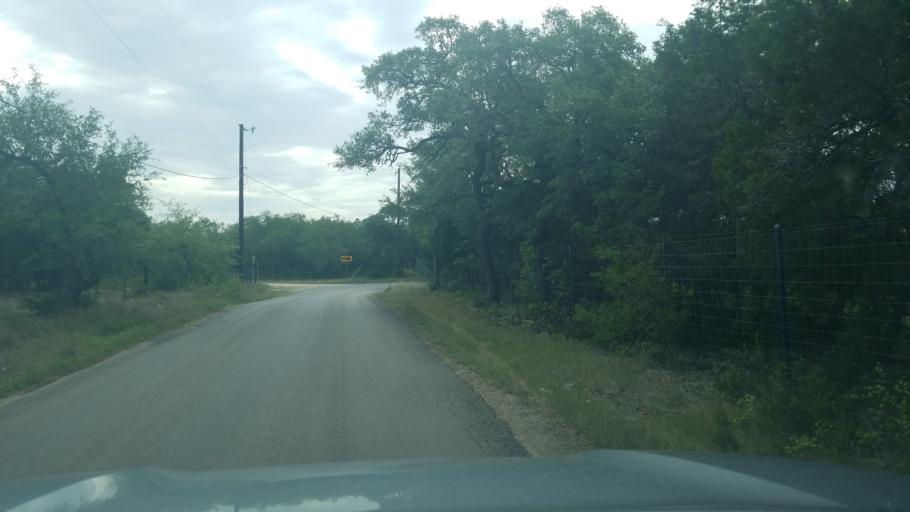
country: US
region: Texas
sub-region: Comal County
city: Bulverde
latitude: 29.7648
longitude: -98.4096
